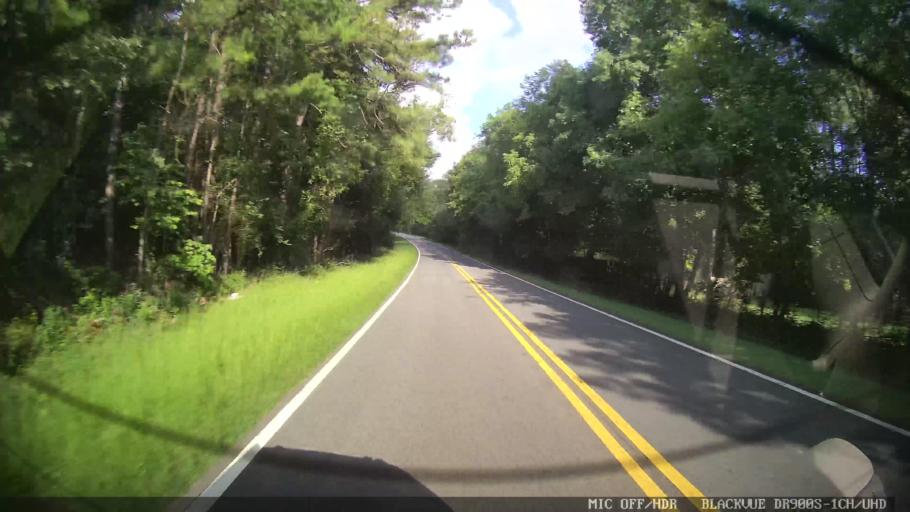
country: US
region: Georgia
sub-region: Bartow County
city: Euharlee
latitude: 34.1776
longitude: -85.0087
